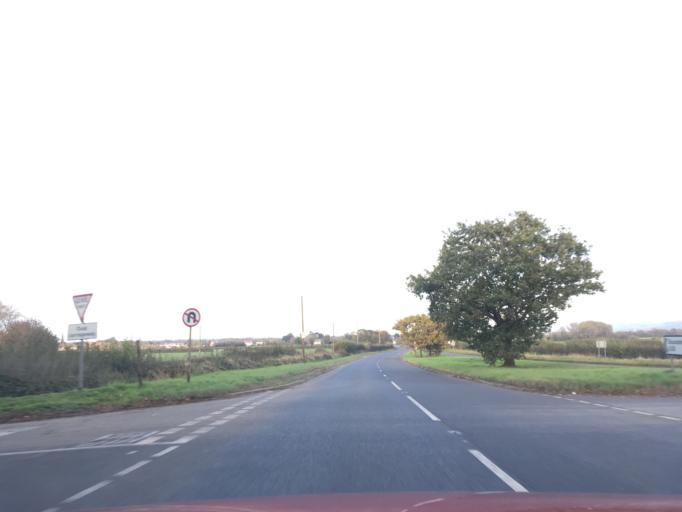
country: GB
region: England
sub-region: Gloucestershire
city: Dursley
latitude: 51.7166
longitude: -2.3793
